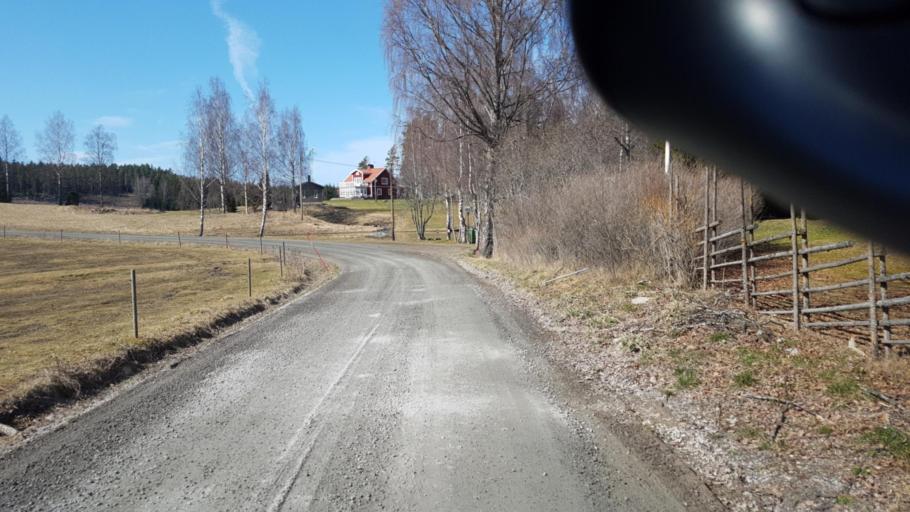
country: SE
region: Vaermland
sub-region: Arvika Kommun
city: Arvika
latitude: 59.5944
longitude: 12.8032
